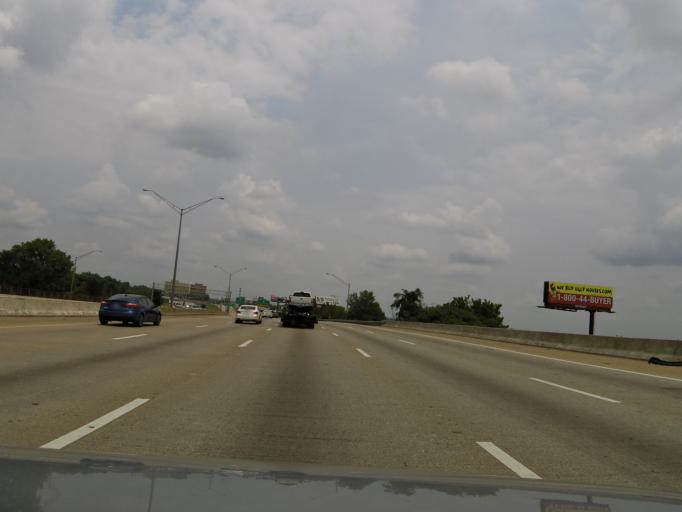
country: US
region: Kentucky
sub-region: Jefferson County
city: Audubon Park
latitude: 38.1913
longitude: -85.7151
